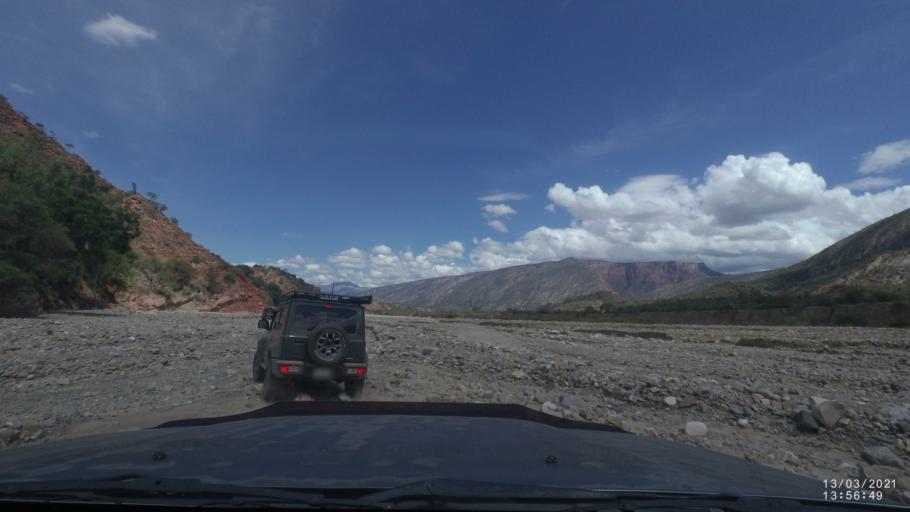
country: BO
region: Cochabamba
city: Cliza
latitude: -17.9349
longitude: -65.8651
